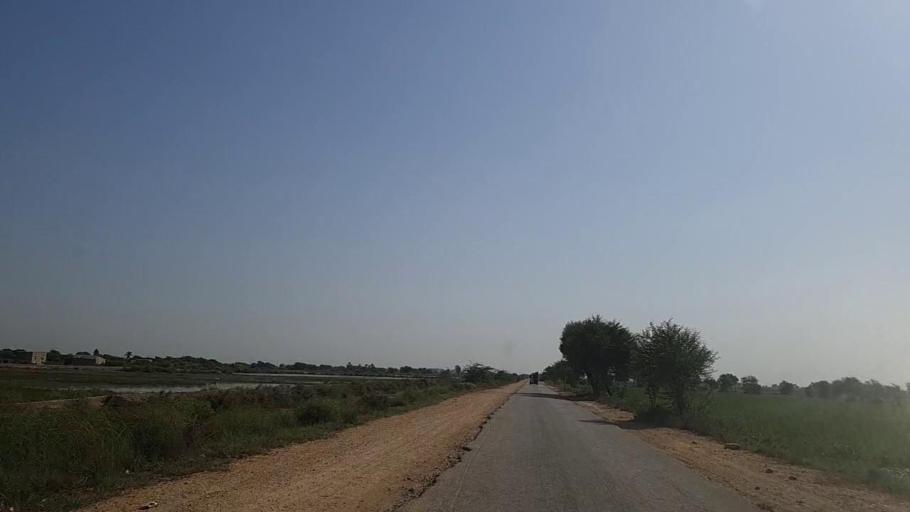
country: PK
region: Sindh
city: Mirpur Batoro
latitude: 24.6538
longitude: 68.2877
